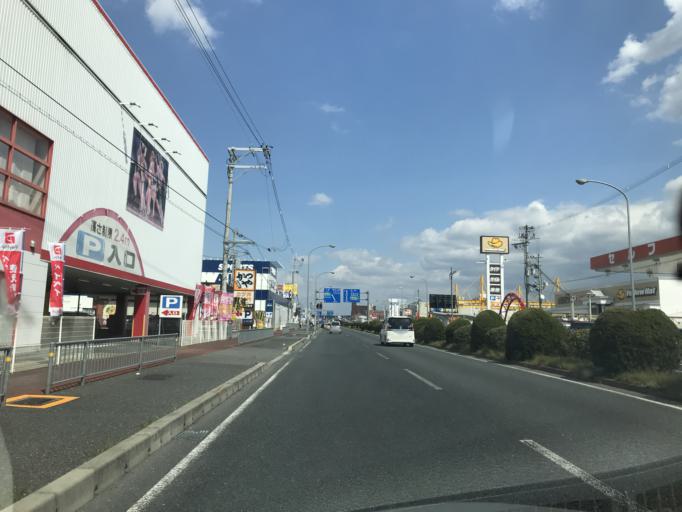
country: JP
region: Nara
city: Nara-shi
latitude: 34.6765
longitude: 135.8004
